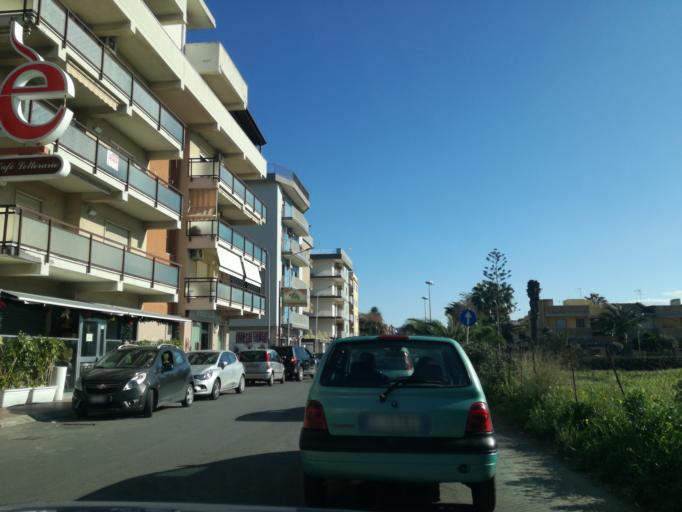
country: IT
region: Sicily
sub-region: Provincia di Caltanissetta
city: Gela
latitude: 37.0727
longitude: 14.2276
